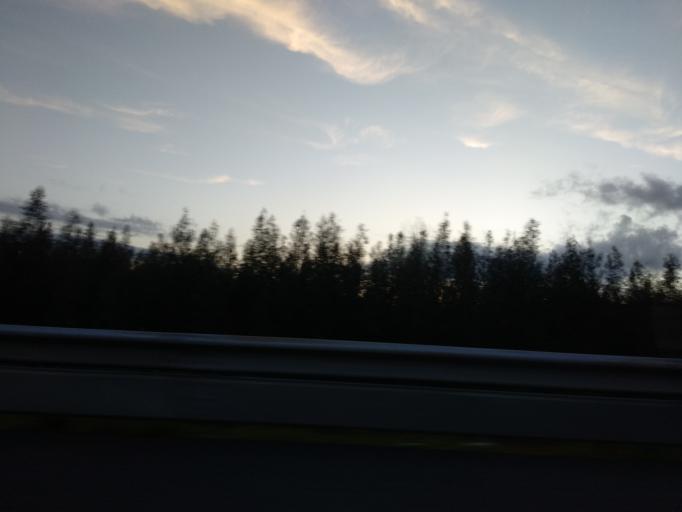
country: PT
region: Braga
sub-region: Vila Nova de Famalicao
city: Vila Nova de Famalicao
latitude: 41.4292
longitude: -8.4977
